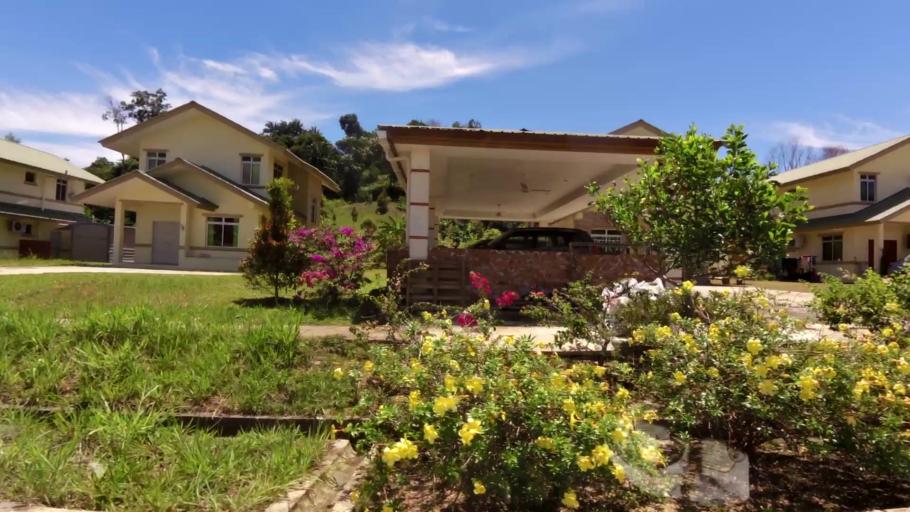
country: BN
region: Brunei and Muara
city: Bandar Seri Begawan
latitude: 5.0272
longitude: 115.0304
